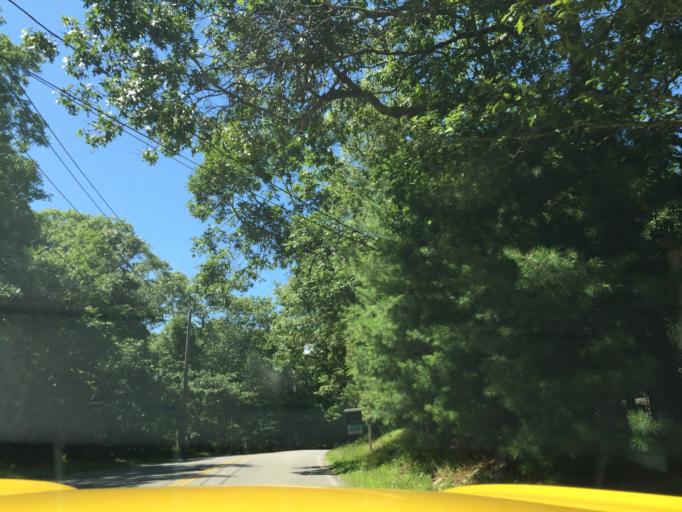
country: US
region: New York
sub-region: Suffolk County
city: Springs
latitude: 41.0058
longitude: -72.1395
